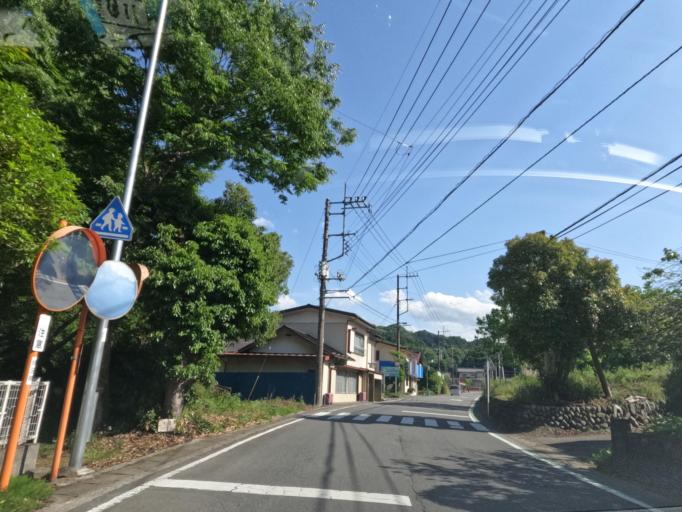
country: JP
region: Saitama
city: Chichibu
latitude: 36.0433
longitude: 139.1308
